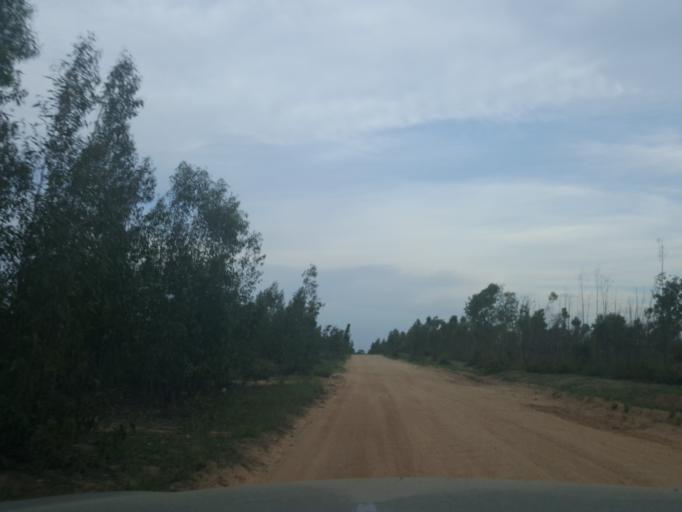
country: ZA
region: Limpopo
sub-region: Mopani District Municipality
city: Hoedspruit
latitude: -24.5878
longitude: 30.9646
